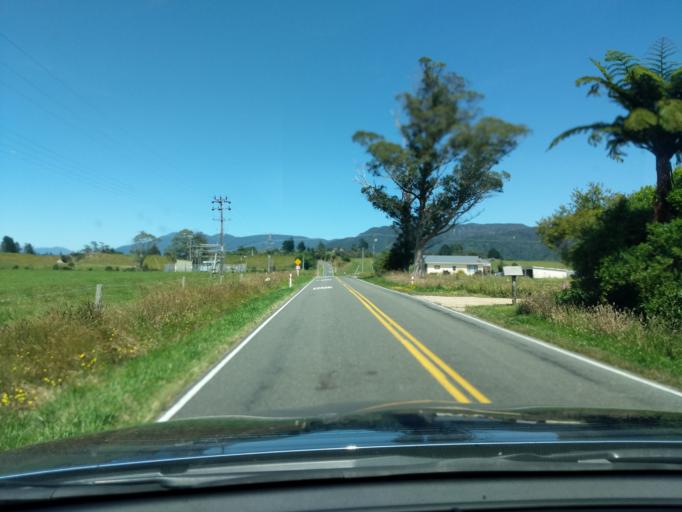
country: NZ
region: Tasman
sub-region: Tasman District
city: Takaka
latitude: -40.6862
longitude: 172.6532
